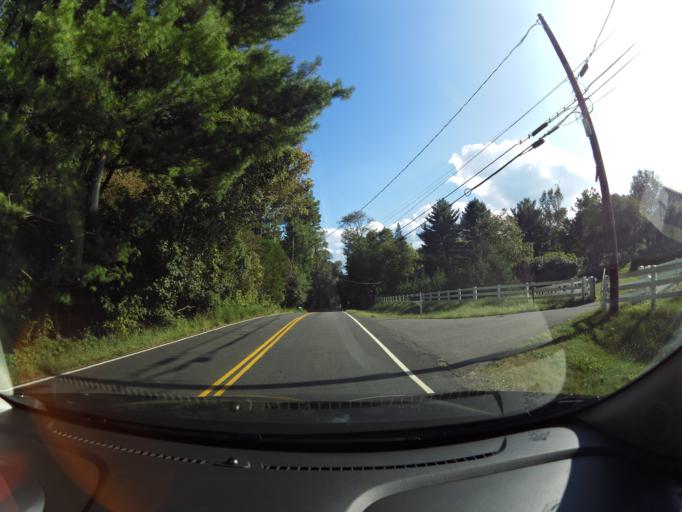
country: US
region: Virginia
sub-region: Fairfax County
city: Tysons Corner
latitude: 38.9697
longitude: -77.2408
